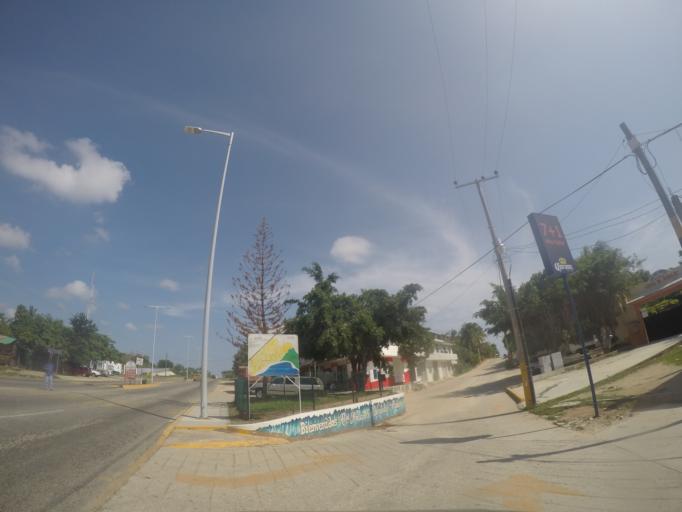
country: MX
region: Oaxaca
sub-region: Santa Maria Colotepec
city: Brisas de Zicatela
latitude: 15.8420
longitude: -97.0434
